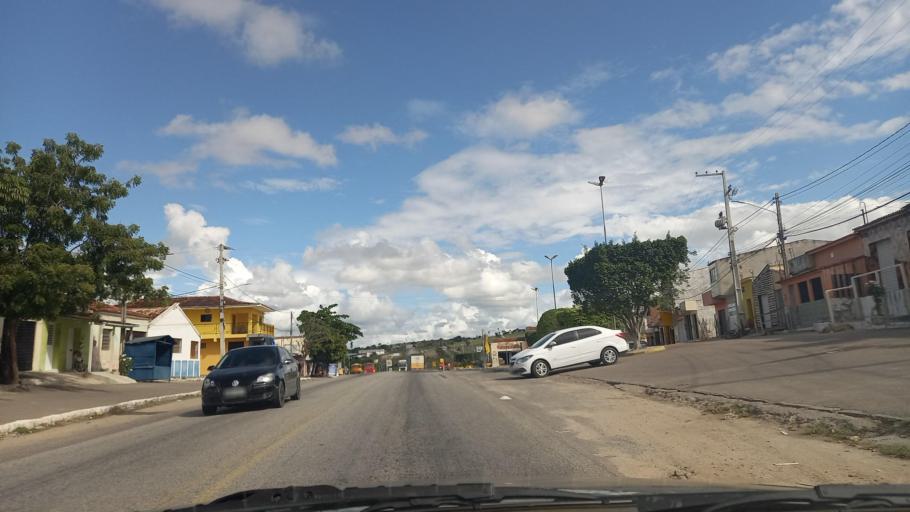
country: BR
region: Pernambuco
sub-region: Sao Joao
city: Sao Joao
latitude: -8.7536
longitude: -36.4309
